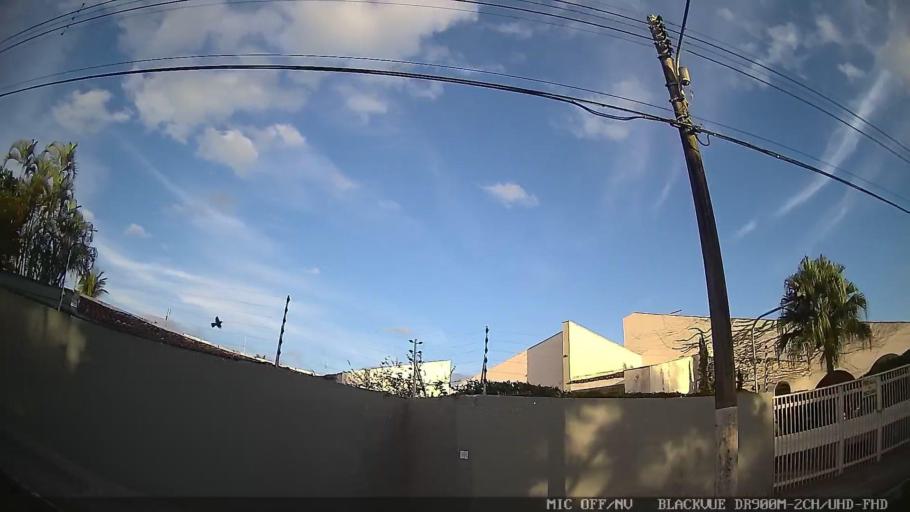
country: BR
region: Sao Paulo
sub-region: Guaruja
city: Guaruja
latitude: -23.9833
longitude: -46.2091
